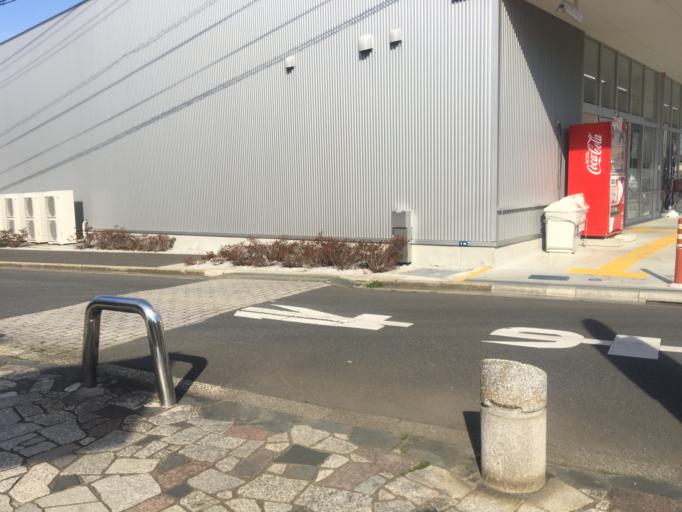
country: JP
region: Saitama
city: Shiki
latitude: 35.8357
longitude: 139.5883
